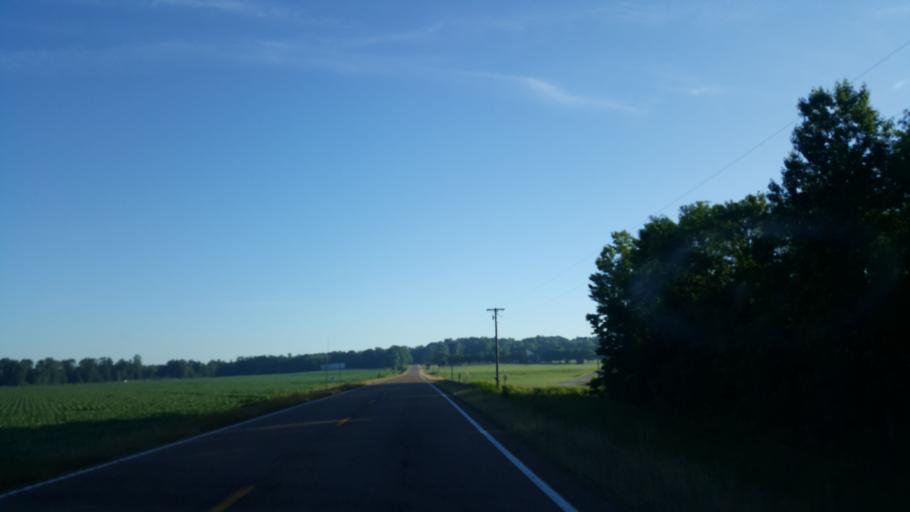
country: US
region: Tennessee
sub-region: McNairy County
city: Adamsville
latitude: 35.4374
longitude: -88.3719
